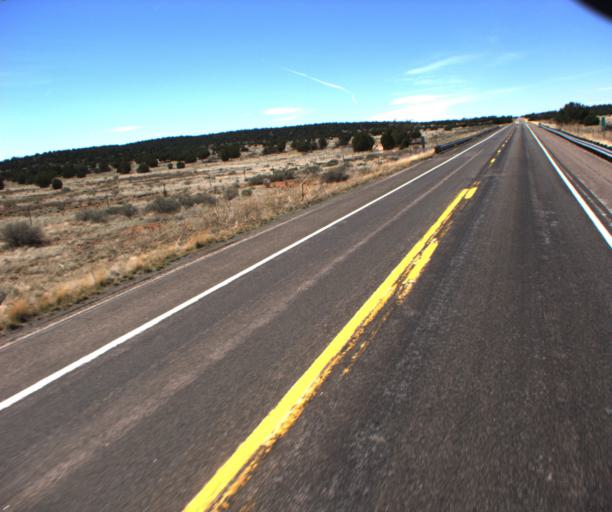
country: US
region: Arizona
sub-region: Mohave County
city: Peach Springs
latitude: 35.5025
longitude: -113.1756
